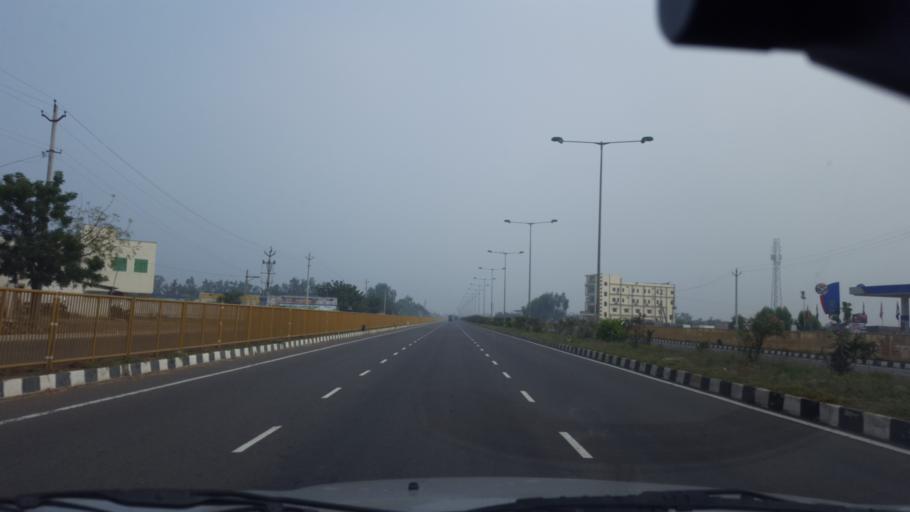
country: IN
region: Andhra Pradesh
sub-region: Guntur
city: Chilakalurupet
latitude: 15.9977
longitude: 80.1099
